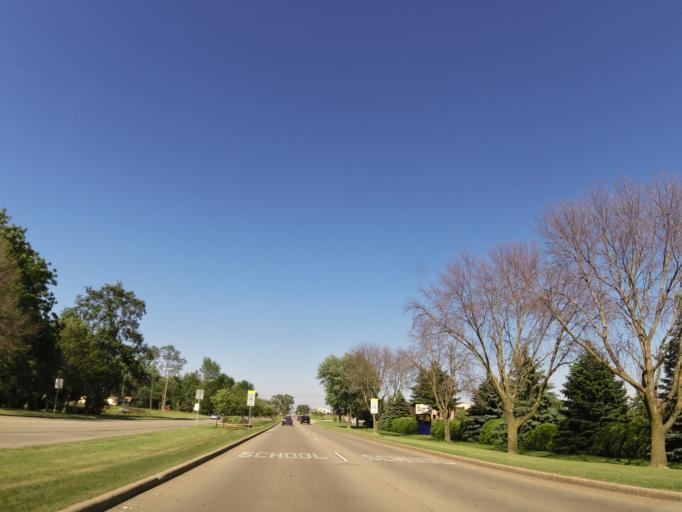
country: US
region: Wisconsin
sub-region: Rock County
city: Beloit
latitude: 42.5190
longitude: -88.9969
